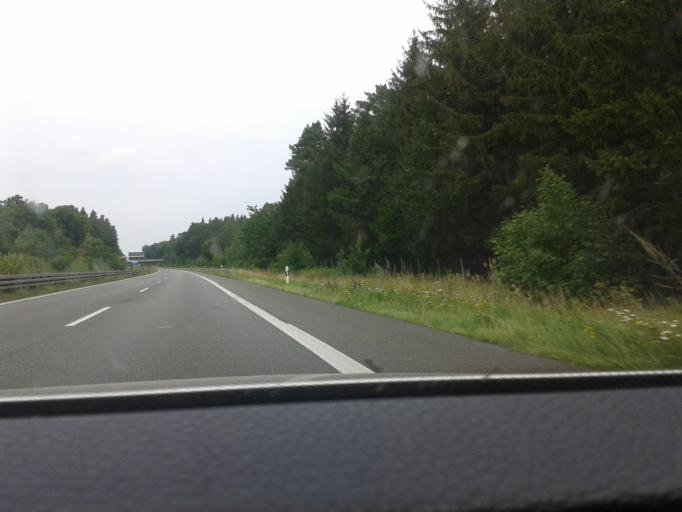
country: DE
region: Lower Saxony
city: Lehre
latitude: 52.3294
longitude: 10.7341
